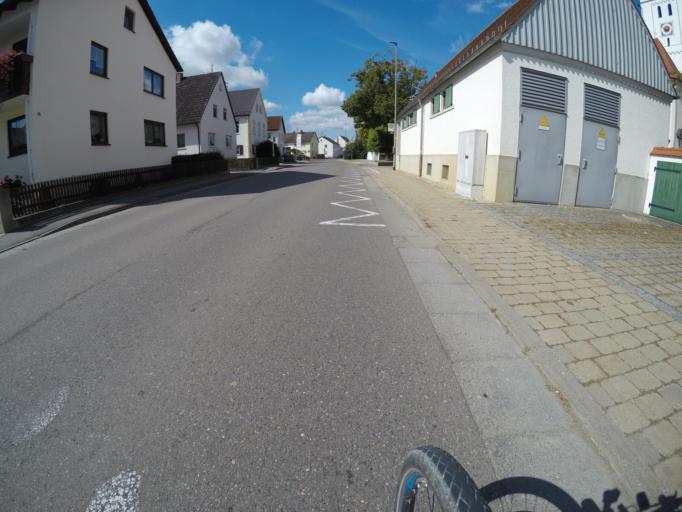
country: DE
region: Bavaria
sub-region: Swabia
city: Finningen
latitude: 48.6228
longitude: 10.5132
